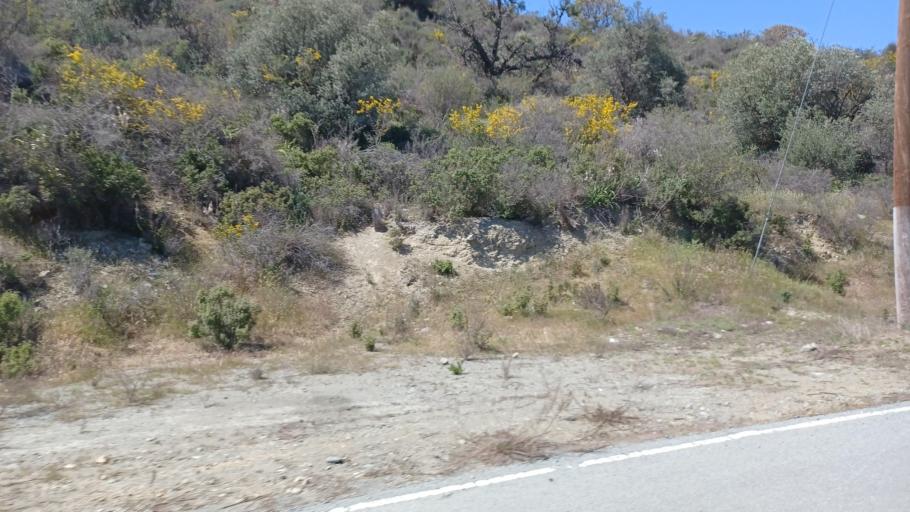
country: CY
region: Limassol
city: Parekklisha
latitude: 34.8067
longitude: 33.1414
